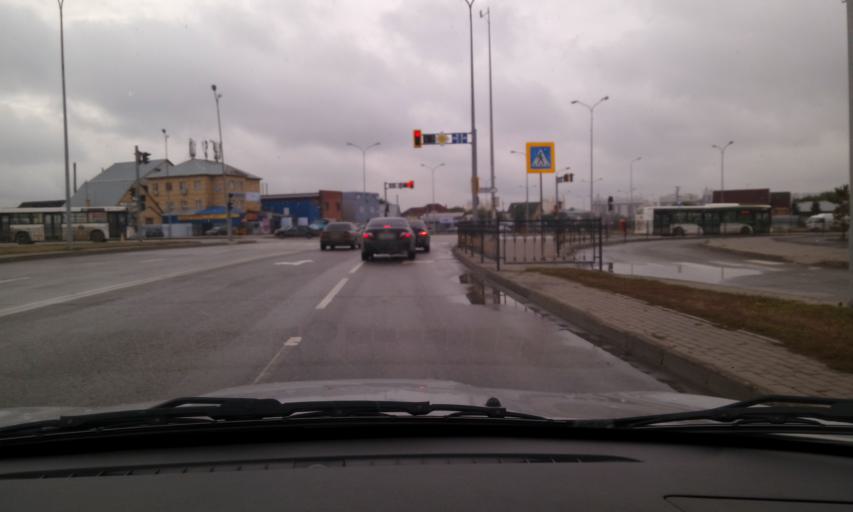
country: KZ
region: Astana Qalasy
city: Astana
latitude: 51.1386
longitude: 71.5195
